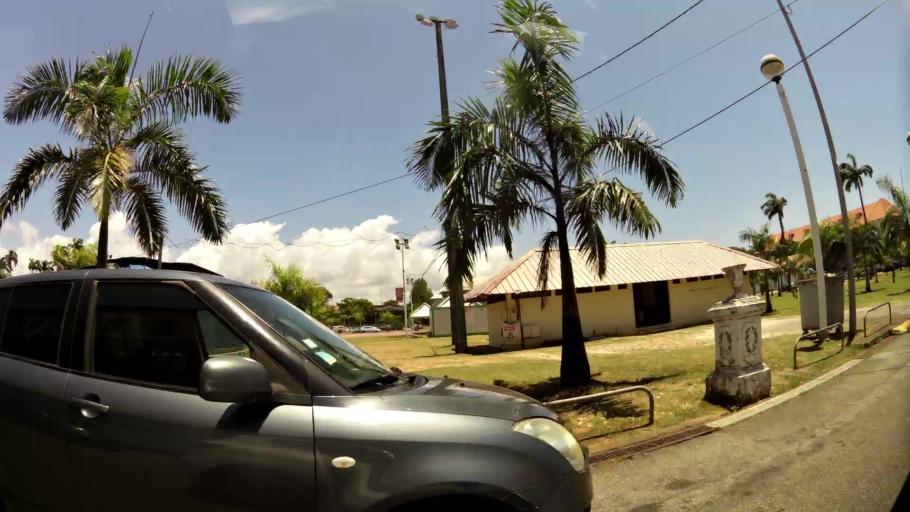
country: GF
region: Guyane
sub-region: Guyane
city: Cayenne
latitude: 4.9403
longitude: -52.3335
